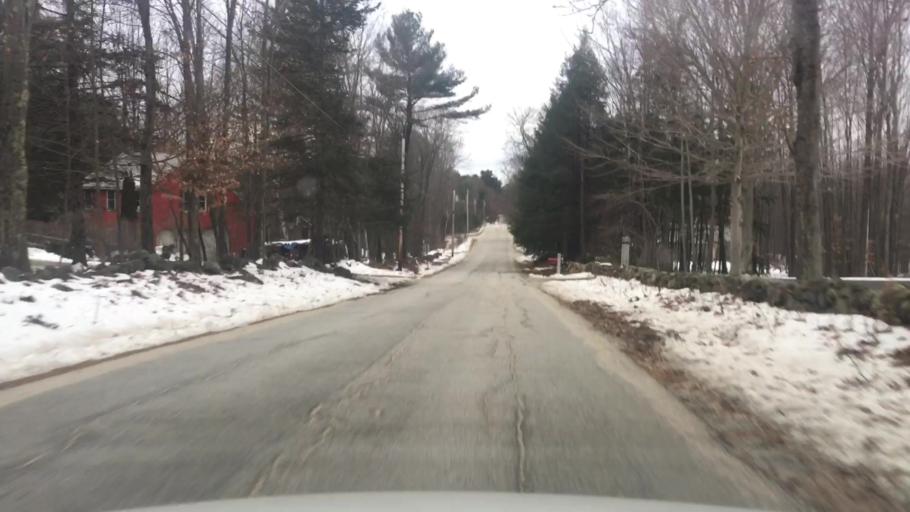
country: US
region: New Hampshire
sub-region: Merrimack County
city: Hopkinton
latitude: 43.1806
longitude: -71.6746
